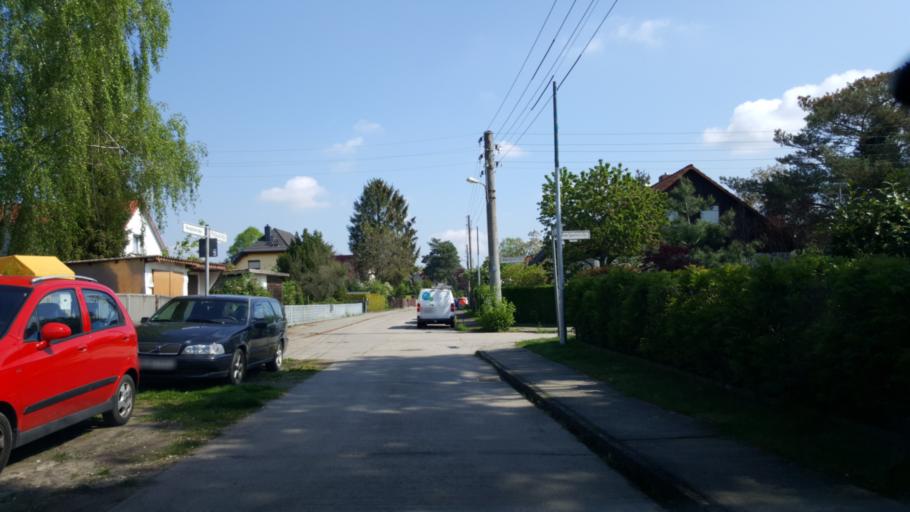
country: DE
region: Berlin
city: Bohnsdorf
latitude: 52.3917
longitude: 13.5603
